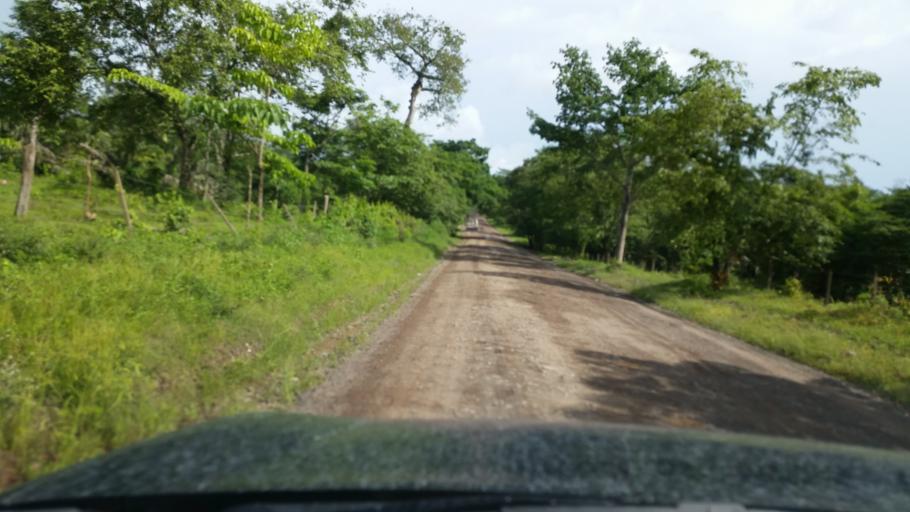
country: NI
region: Atlantico Norte (RAAN)
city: Siuna
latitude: 13.6862
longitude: -84.7898
